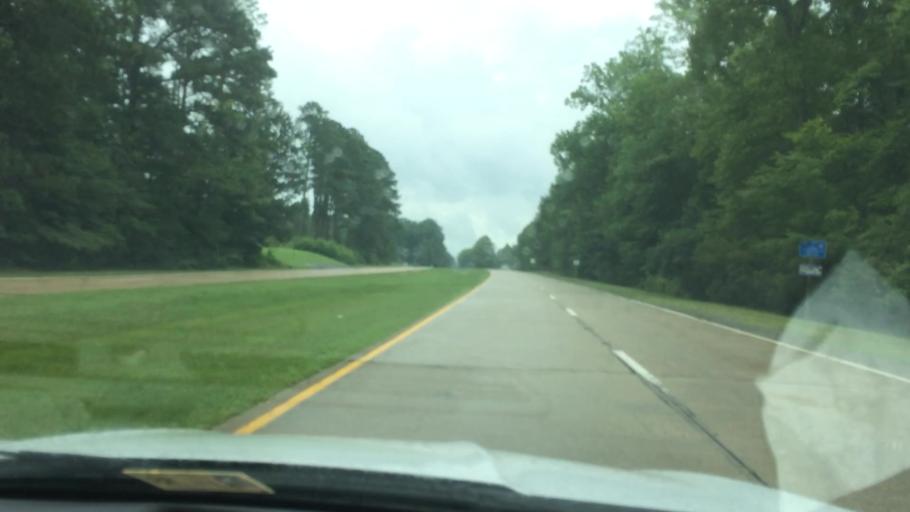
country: US
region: Virginia
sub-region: New Kent County
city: New Kent
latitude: 37.4391
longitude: -77.0266
